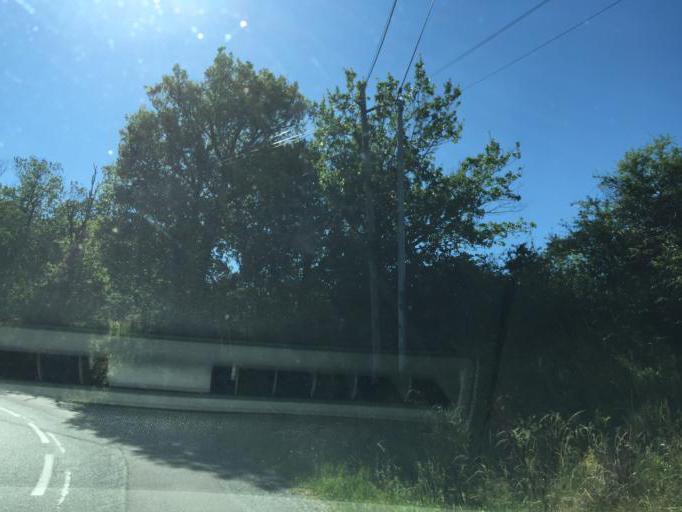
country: FR
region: Rhone-Alpes
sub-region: Departement du Rhone
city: Saint-Andeol-le-Chateau
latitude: 45.5660
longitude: 4.6995
